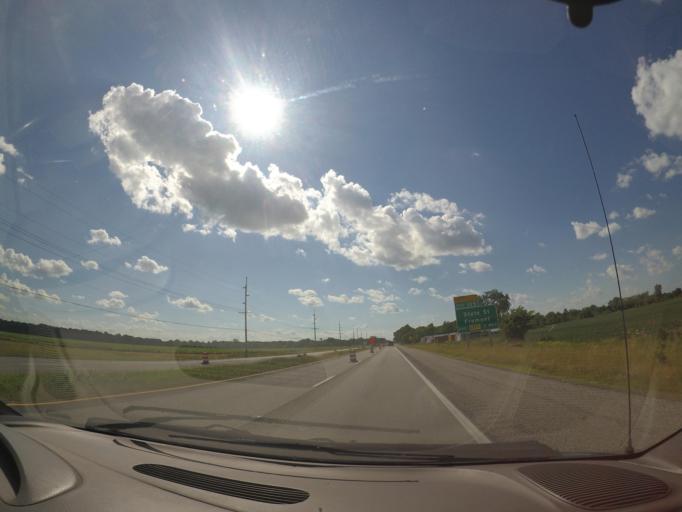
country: US
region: Ohio
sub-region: Sandusky County
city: Clyde
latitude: 41.3273
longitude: -83.0382
